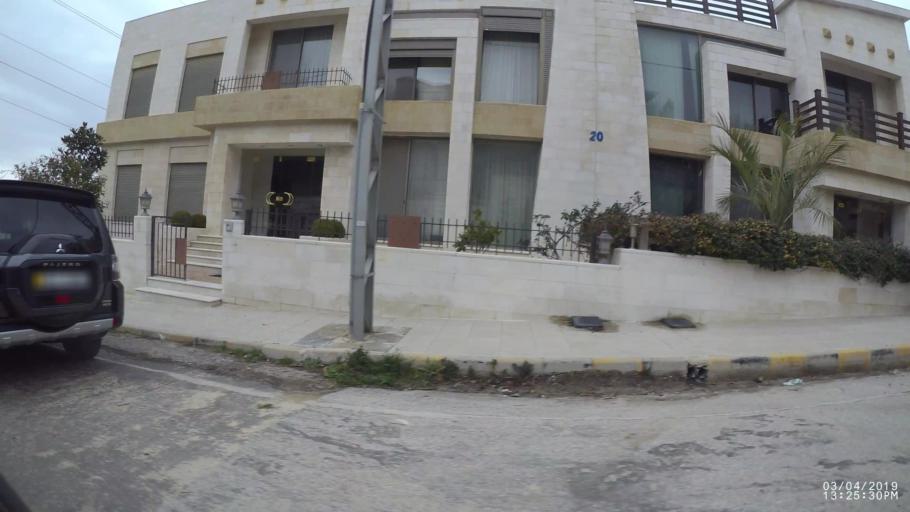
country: JO
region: Amman
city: Wadi as Sir
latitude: 31.9659
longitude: 35.8227
